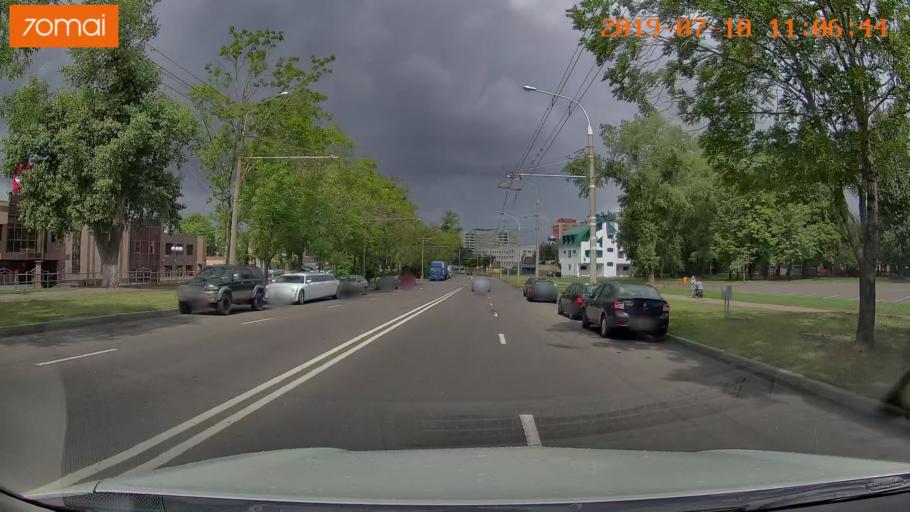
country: BY
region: Minsk
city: Syenitsa
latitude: 53.8486
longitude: 27.5426
